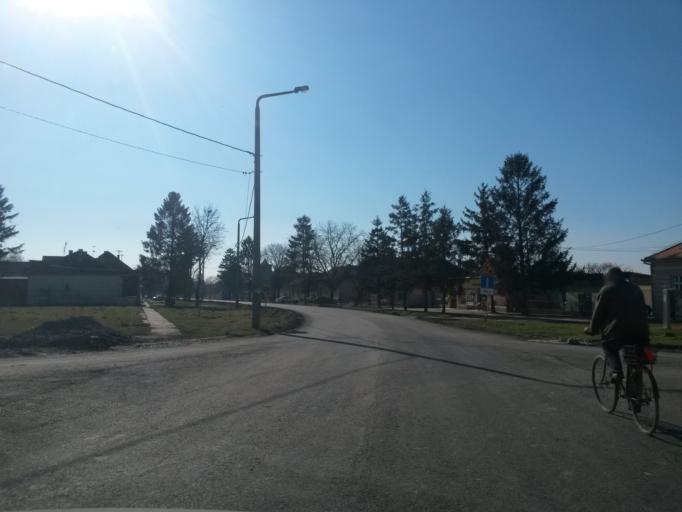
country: HR
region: Vukovarsko-Srijemska
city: Negoslavci
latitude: 45.2783
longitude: 18.9973
